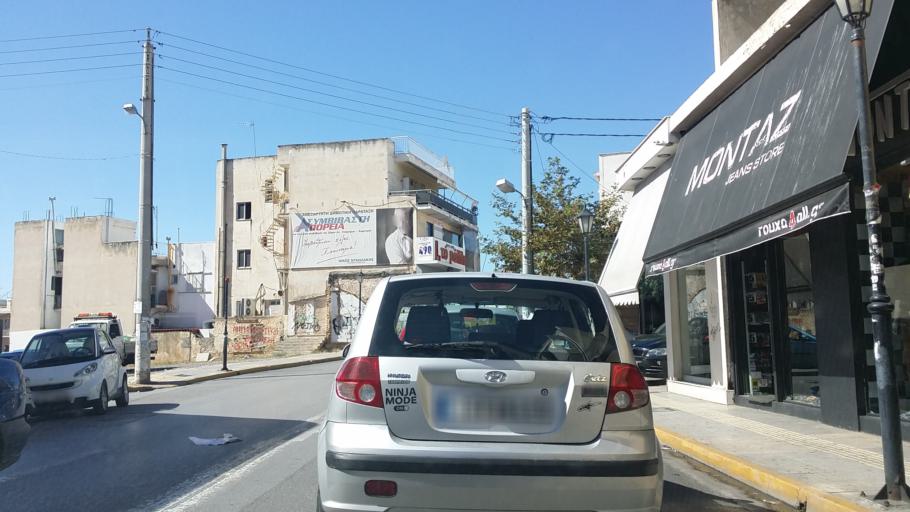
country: GR
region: Attica
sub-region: Nomarchia Athinas
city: Agioi Anargyroi
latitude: 38.0275
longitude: 23.7206
